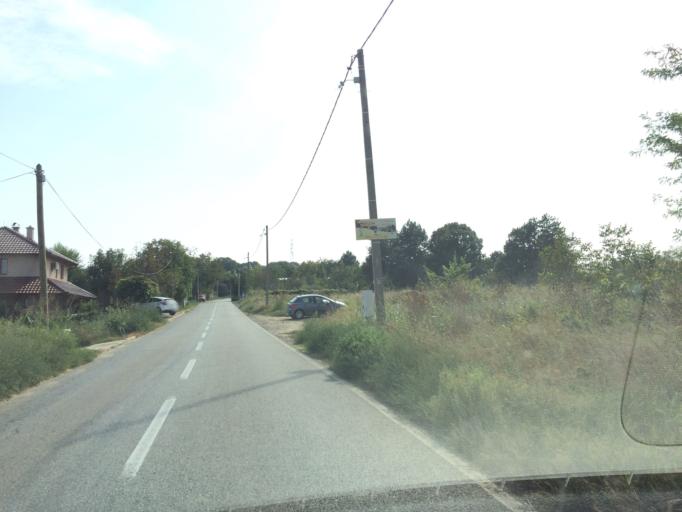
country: RS
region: Autonomna Pokrajina Vojvodina
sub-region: Juznobacki Okrug
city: Novi Sad
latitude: 45.2137
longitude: 19.8350
